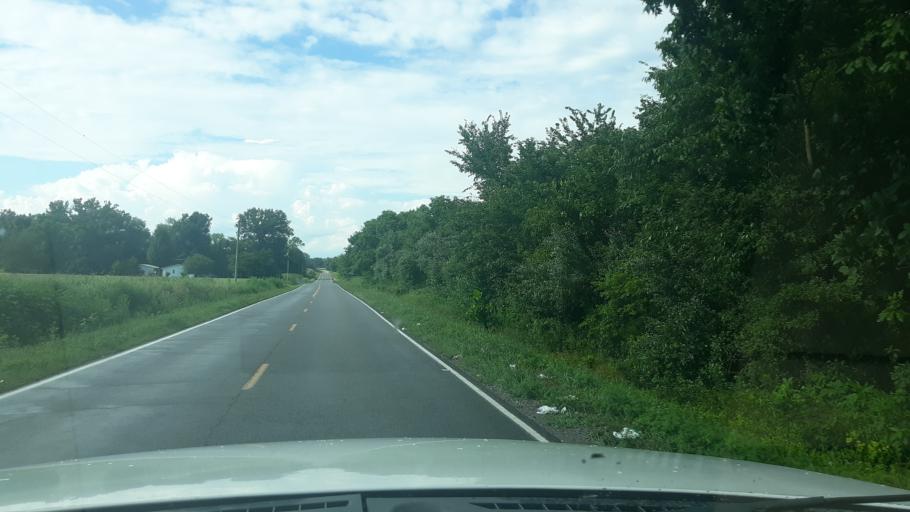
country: US
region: Illinois
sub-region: Saline County
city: Eldorado
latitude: 37.8506
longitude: -88.5304
